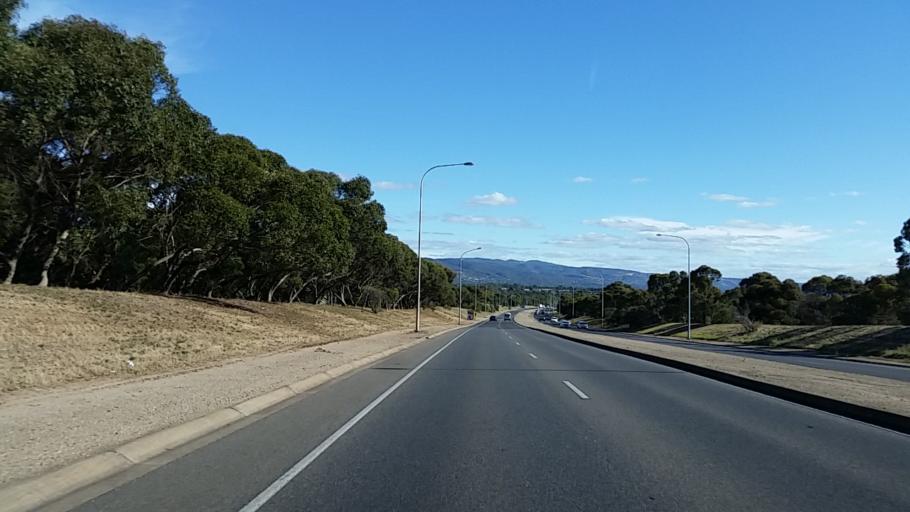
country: AU
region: South Australia
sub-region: Tea Tree Gully
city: Modbury
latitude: -34.8218
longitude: 138.6786
